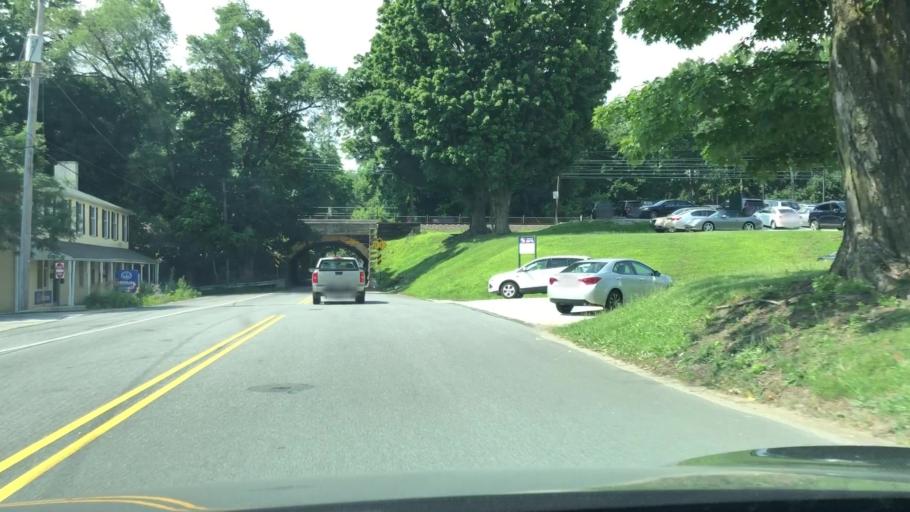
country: US
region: Pennsylvania
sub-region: Chester County
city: Devon
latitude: 40.0465
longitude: -75.4237
